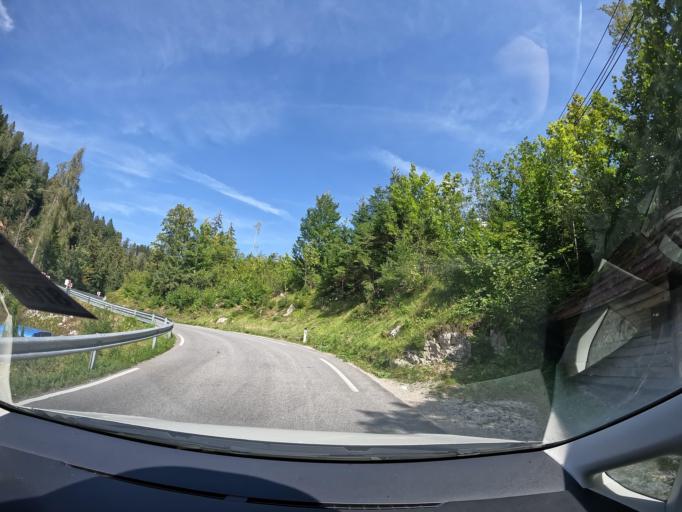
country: AT
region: Carinthia
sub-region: Politischer Bezirk Villach Land
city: Velden am Woerthersee
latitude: 46.5931
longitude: 14.0644
